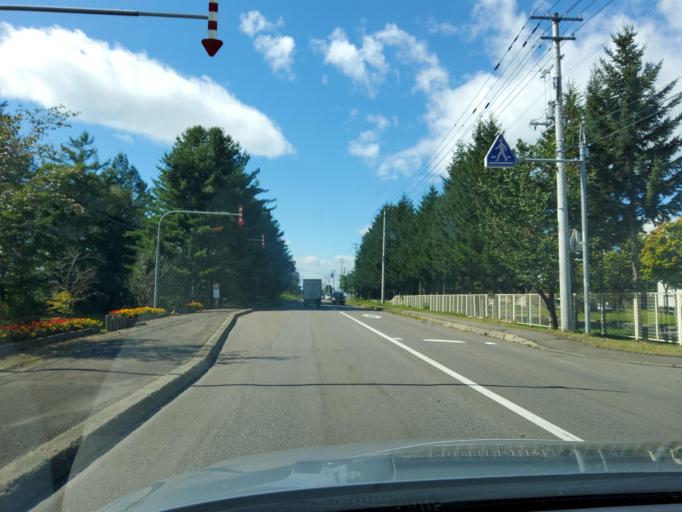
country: JP
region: Hokkaido
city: Obihiro
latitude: 42.9368
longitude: 143.2890
